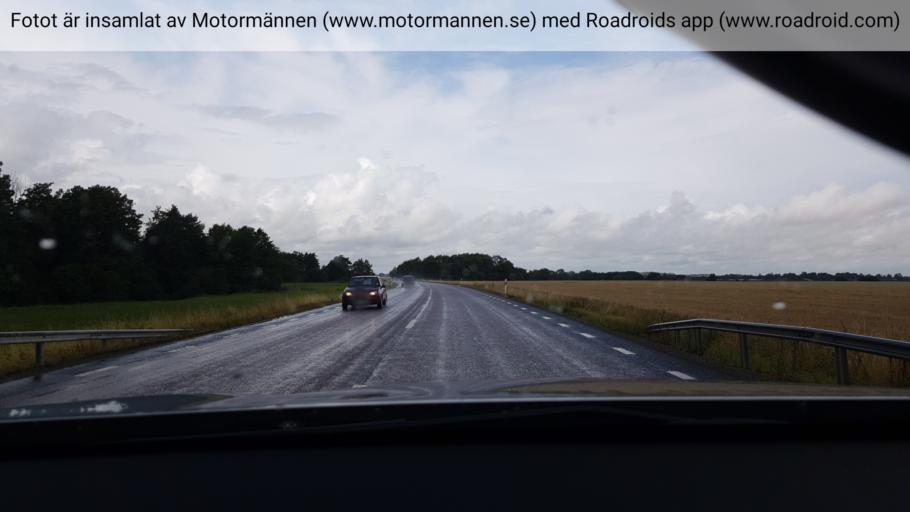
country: SE
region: Uppsala
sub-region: Uppsala Kommun
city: Gamla Uppsala
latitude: 59.9090
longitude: 17.5369
